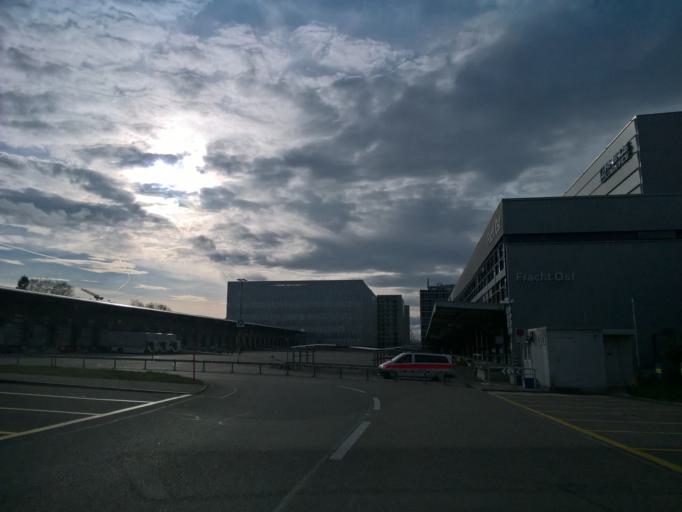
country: CH
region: Zurich
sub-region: Bezirk Buelach
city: Kloten / Holberg
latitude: 47.4531
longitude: 8.5720
